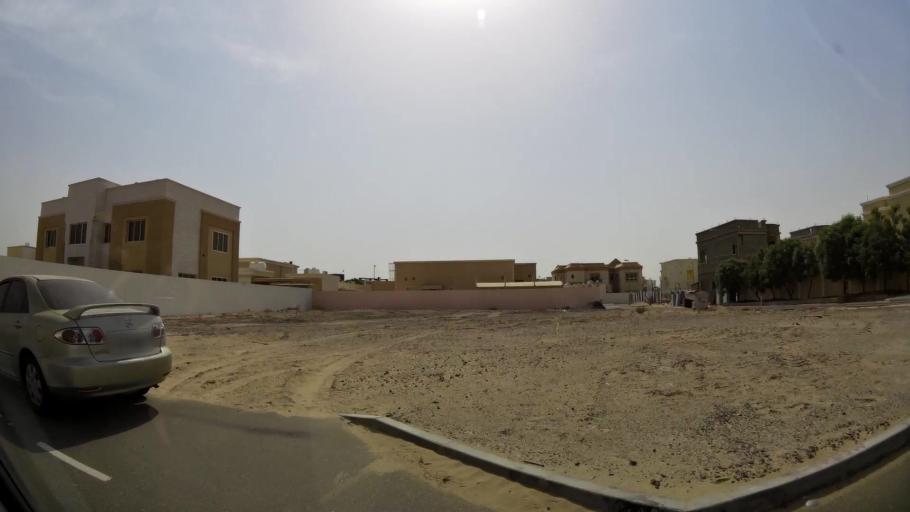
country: AE
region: Ash Shariqah
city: Sharjah
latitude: 25.2582
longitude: 55.4646
